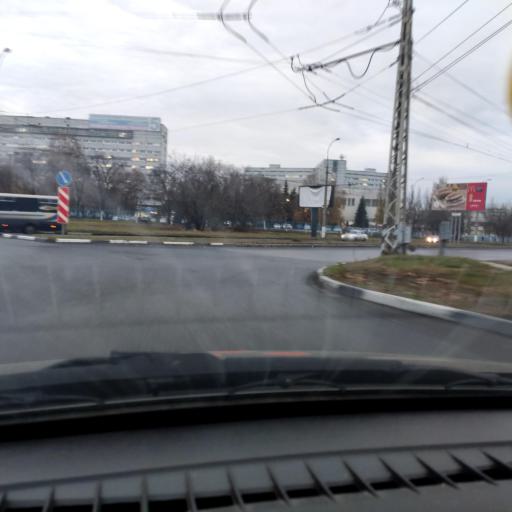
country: RU
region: Samara
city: Tol'yatti
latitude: 53.5246
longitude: 49.3255
